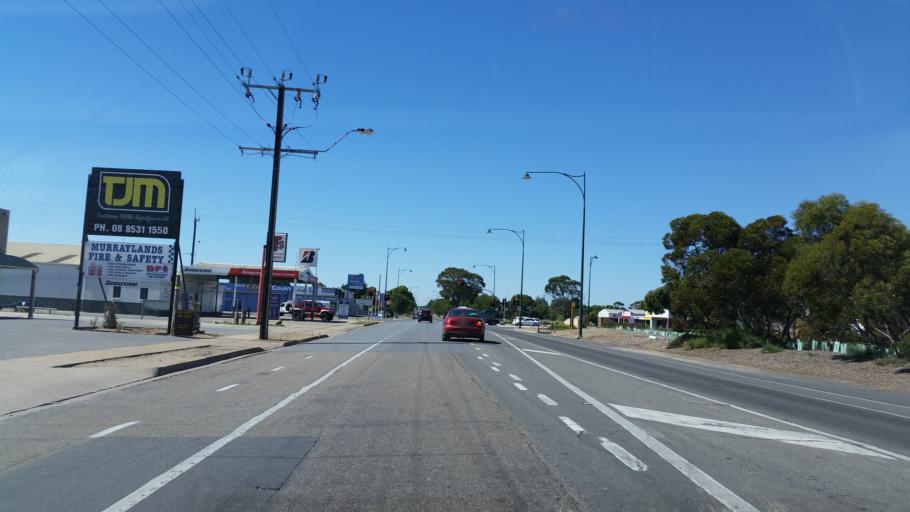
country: AU
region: South Australia
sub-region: Murray Bridge
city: Murray Bridge
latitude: -35.1270
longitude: 139.2563
